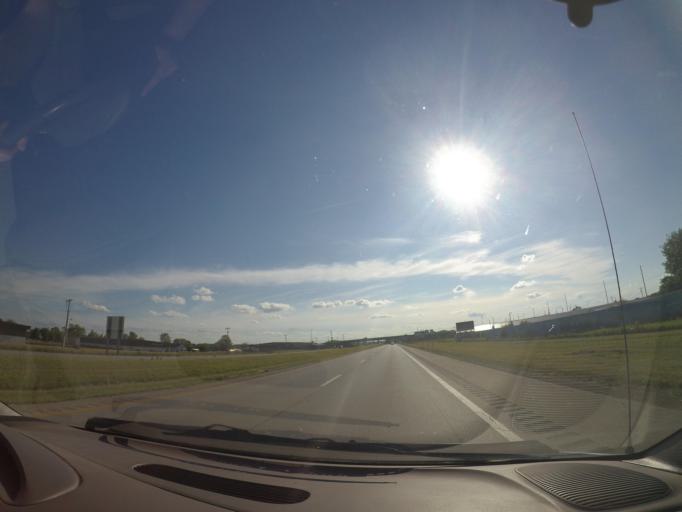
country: US
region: Ohio
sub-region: Henry County
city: Napoleon
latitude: 41.4126
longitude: -84.1155
